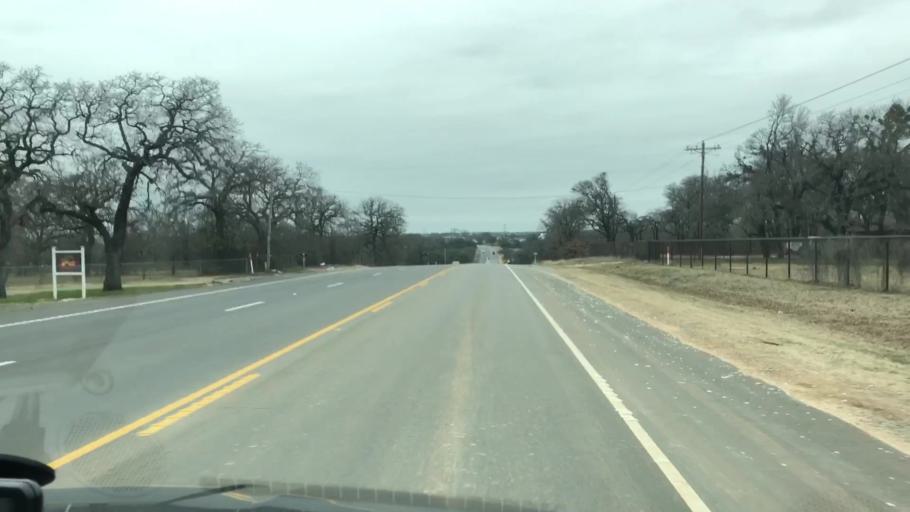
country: US
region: Texas
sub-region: Erath County
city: Stephenville
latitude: 32.1804
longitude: -98.1629
